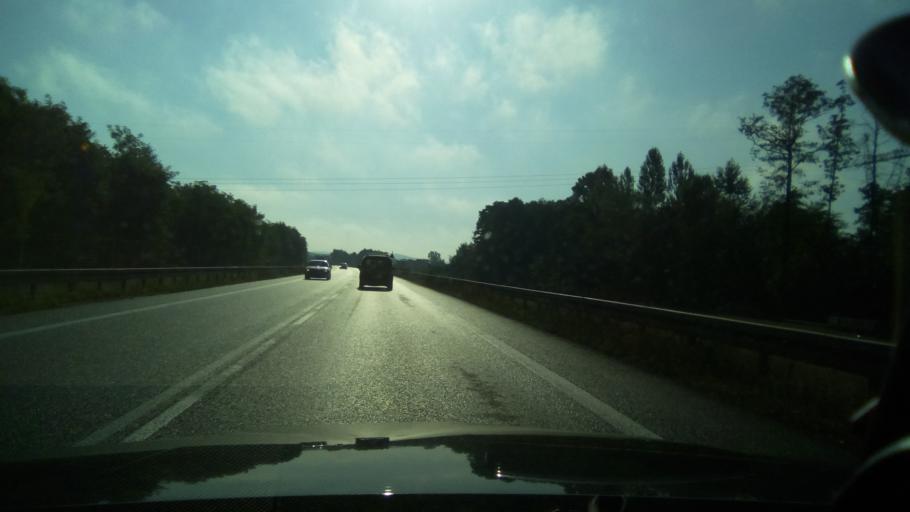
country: PL
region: Silesian Voivodeship
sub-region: Powiat bedzinski
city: Siewierz
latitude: 50.4214
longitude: 19.1891
